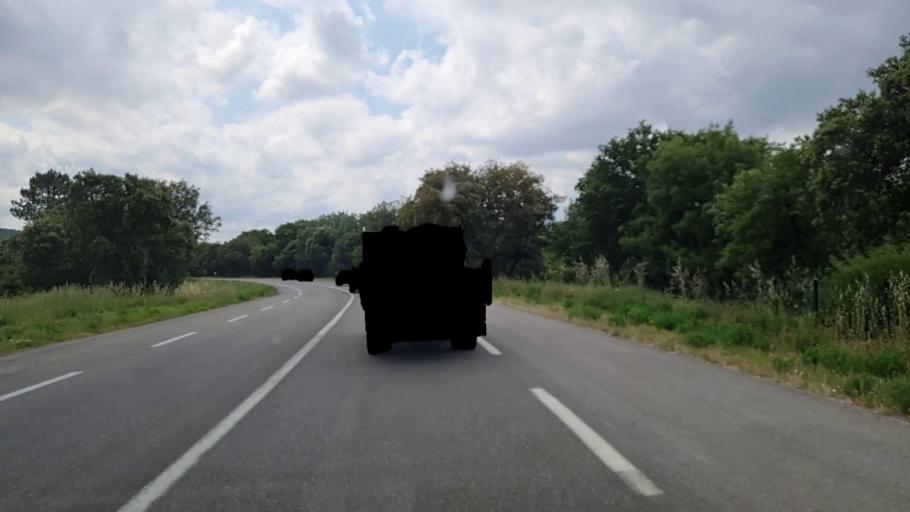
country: FR
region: Languedoc-Roussillon
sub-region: Departement du Gard
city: Quissac
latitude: 43.9290
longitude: 3.9799
